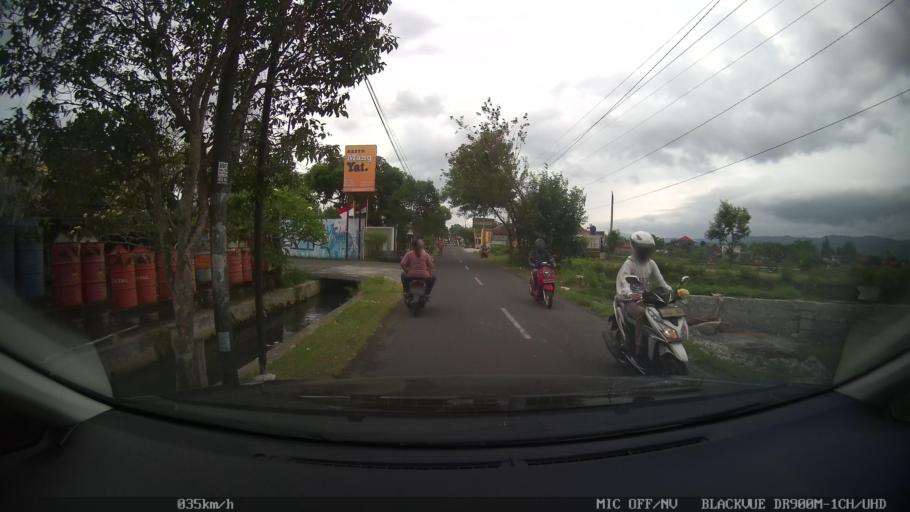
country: ID
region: Daerah Istimewa Yogyakarta
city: Sewon
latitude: -7.8360
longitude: 110.4175
